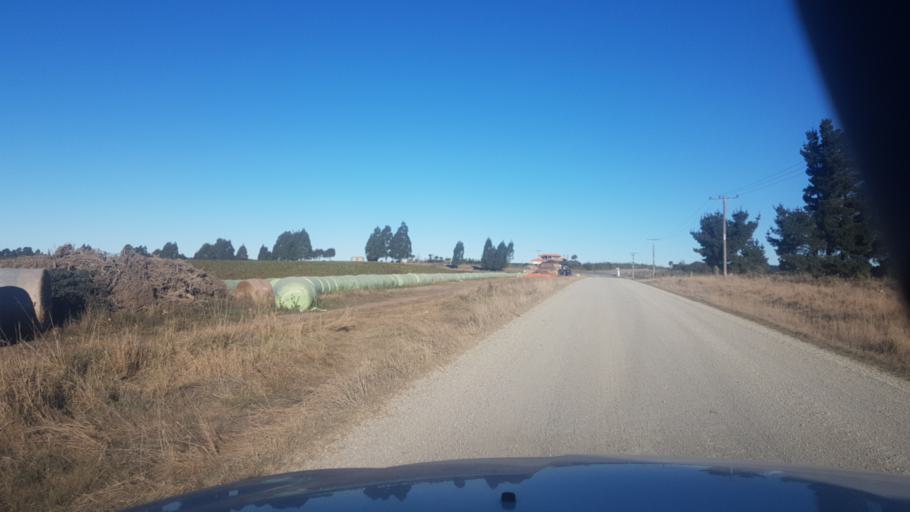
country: NZ
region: Canterbury
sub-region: Timaru District
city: Pleasant Point
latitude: -44.3574
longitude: 171.0693
